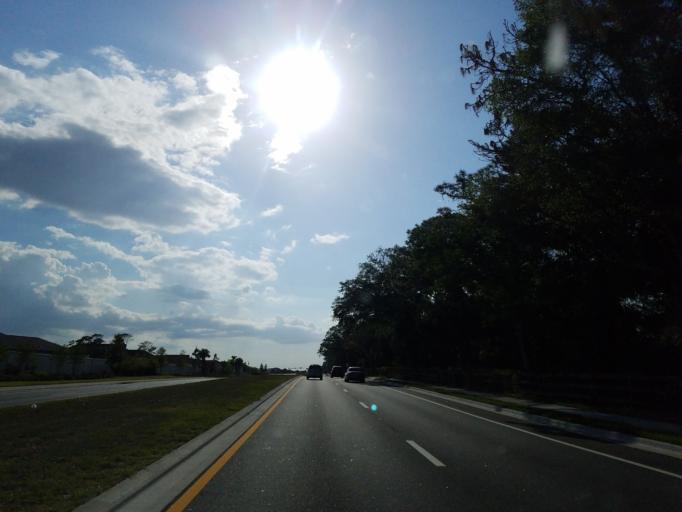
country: US
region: Florida
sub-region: Lake County
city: Fruitland Park
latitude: 28.8617
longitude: -81.9389
